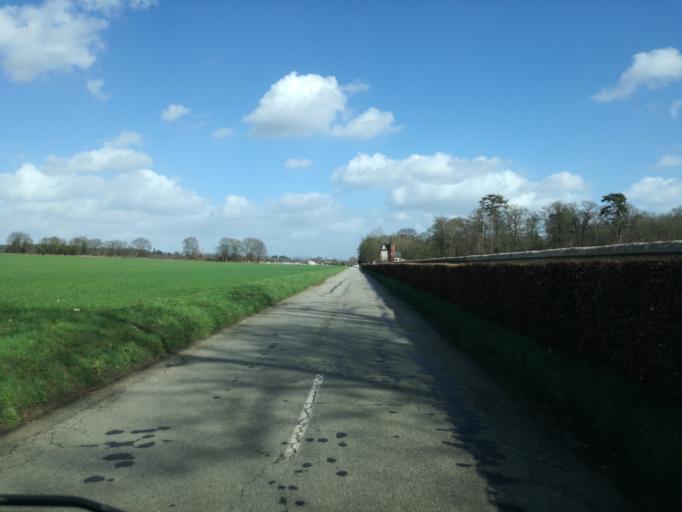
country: FR
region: Haute-Normandie
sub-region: Departement de la Seine-Maritime
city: Sahurs
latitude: 49.3577
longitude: 0.9626
